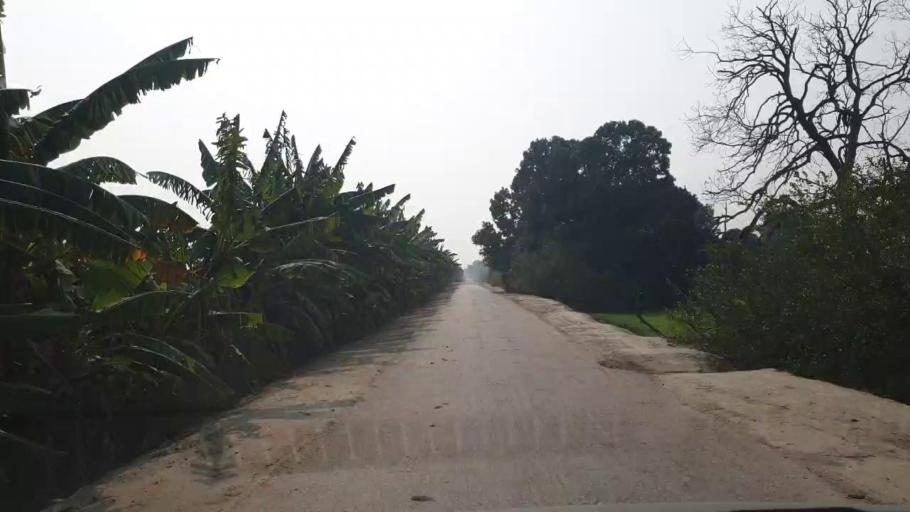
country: PK
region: Sindh
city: Hala
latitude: 25.8187
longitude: 68.4374
